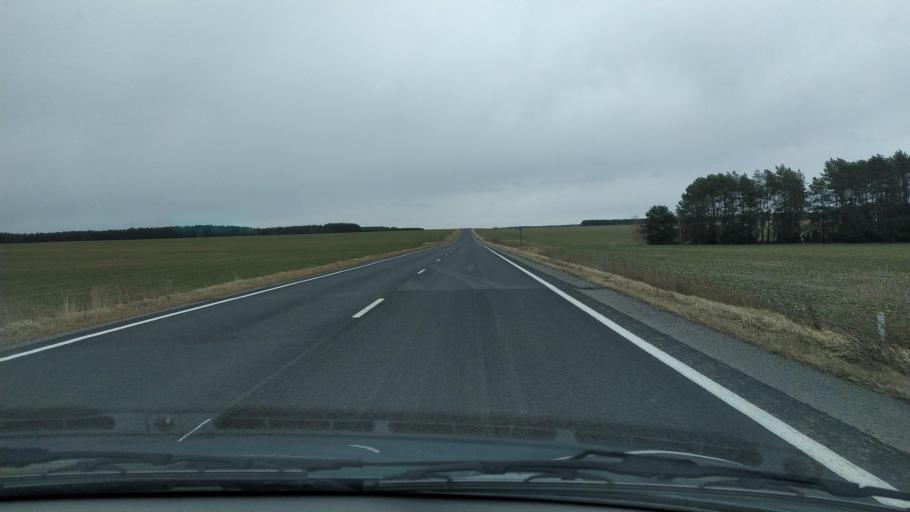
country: BY
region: Brest
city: Kamyanyets
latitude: 52.3946
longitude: 23.9295
